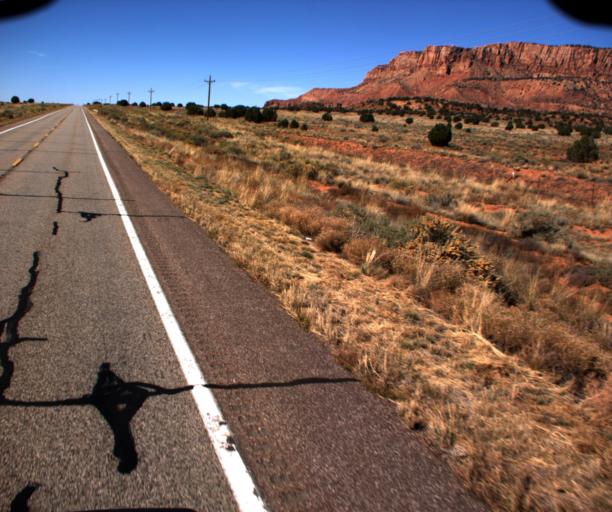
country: US
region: Arizona
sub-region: Mohave County
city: Colorado City
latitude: 36.8581
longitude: -112.7807
